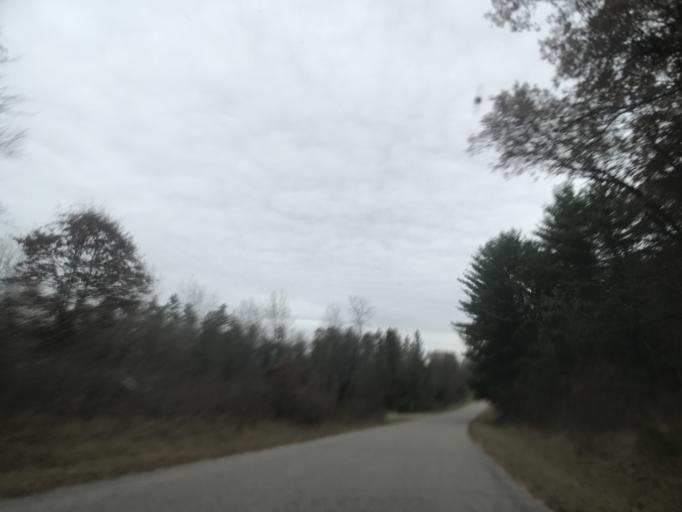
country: US
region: Wisconsin
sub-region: Oconto County
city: Gillett
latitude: 45.3471
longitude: -88.2860
